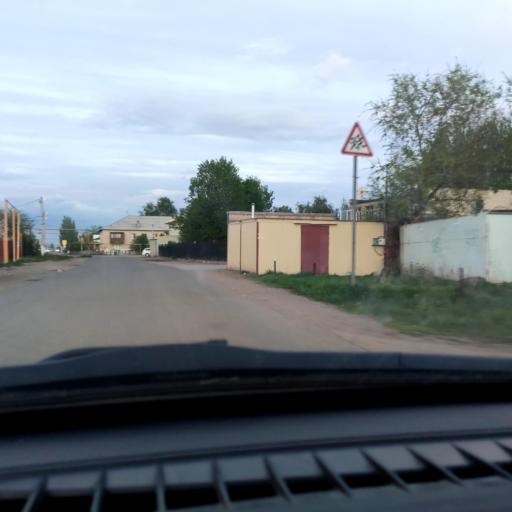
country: RU
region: Samara
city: Podstepki
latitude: 53.5166
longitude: 49.1128
